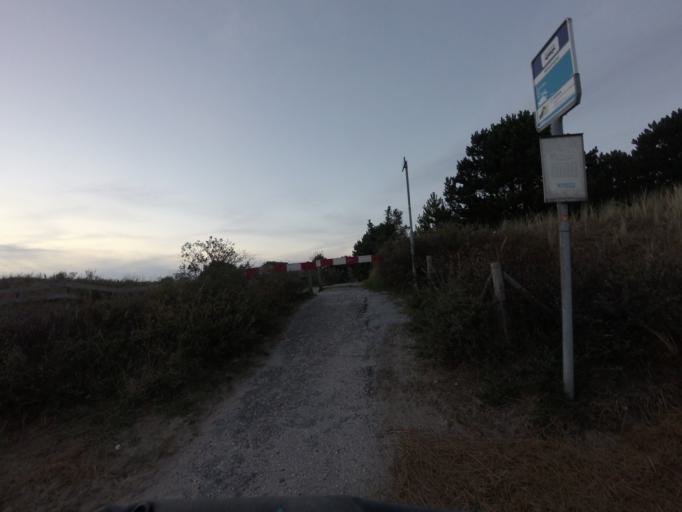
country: NL
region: Friesland
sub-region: Gemeente Ameland
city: Nes
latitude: 53.4557
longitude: 5.7959
